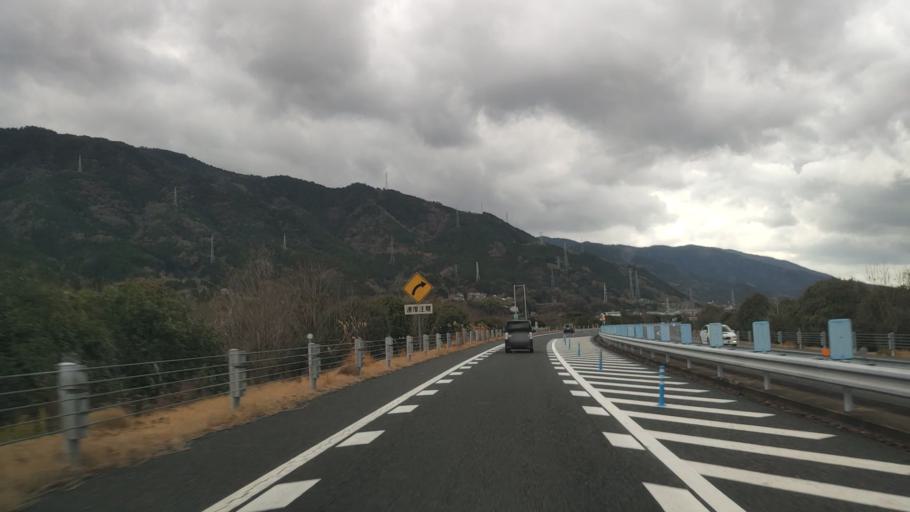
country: JP
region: Tokushima
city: Ikedacho
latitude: 34.0380
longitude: 133.9058
